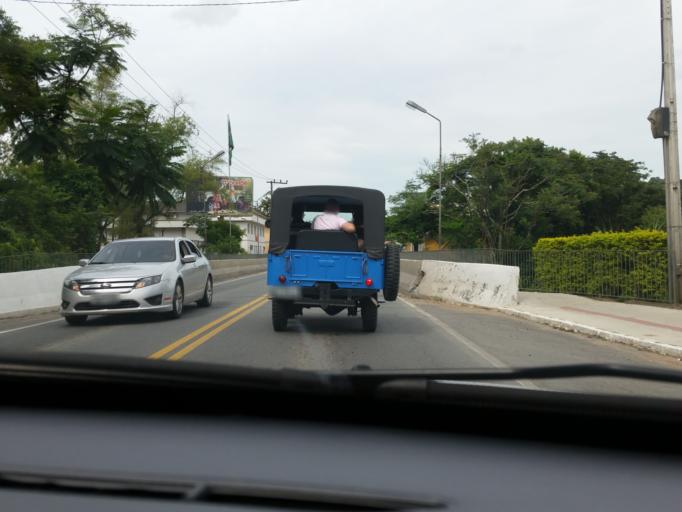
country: BR
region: Santa Catarina
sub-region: Rodeio
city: Gavea
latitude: -27.0351
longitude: -49.3893
